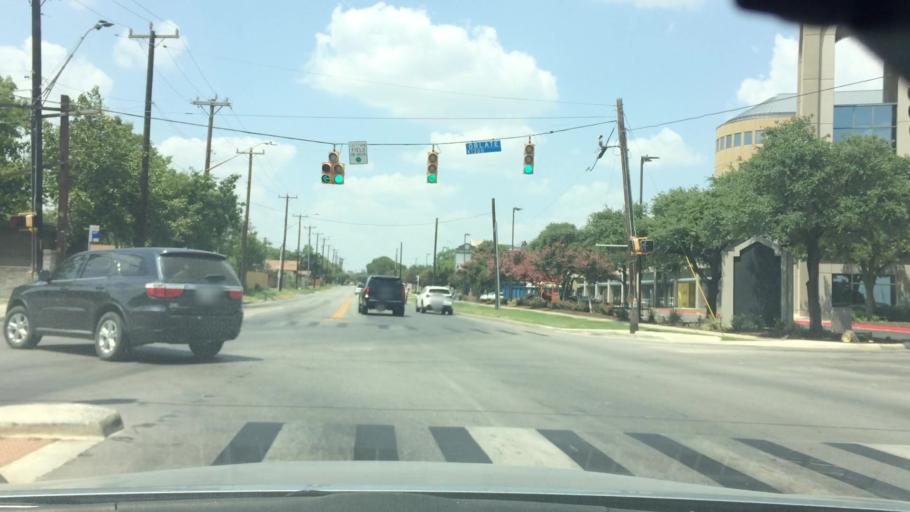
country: US
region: Texas
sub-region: Bexar County
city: Alamo Heights
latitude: 29.5041
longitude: -98.4817
